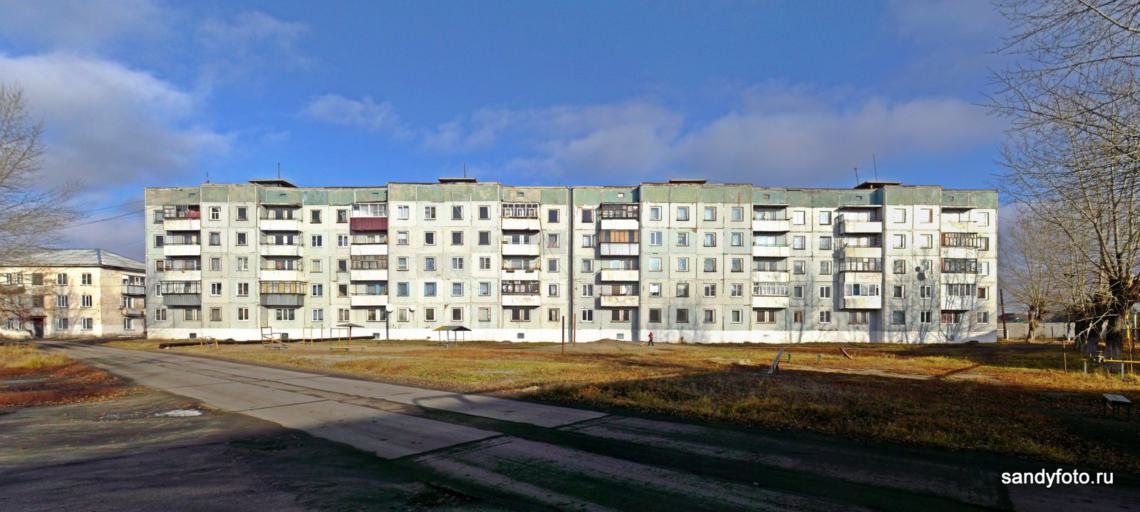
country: RU
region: Chelyabinsk
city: Troitsk
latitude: 54.1076
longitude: 61.5543
